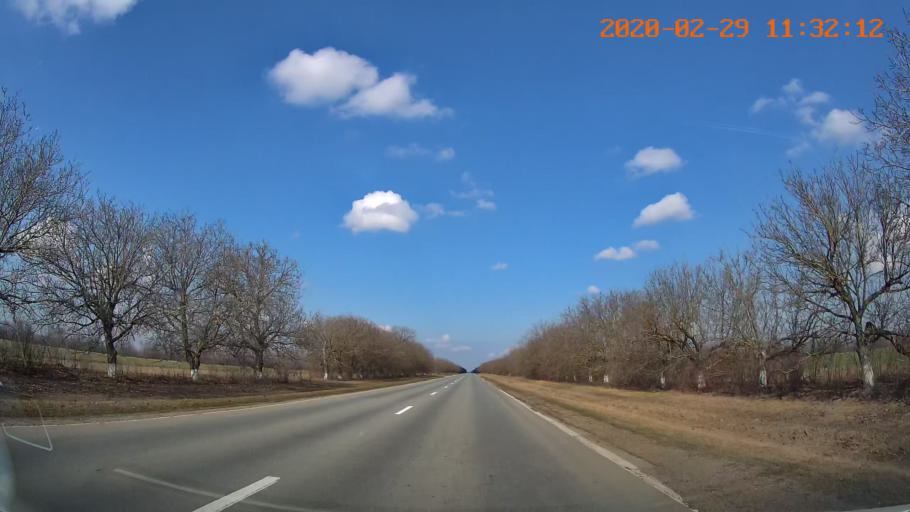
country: MD
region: Rezina
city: Saharna
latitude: 47.5346
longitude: 29.0969
